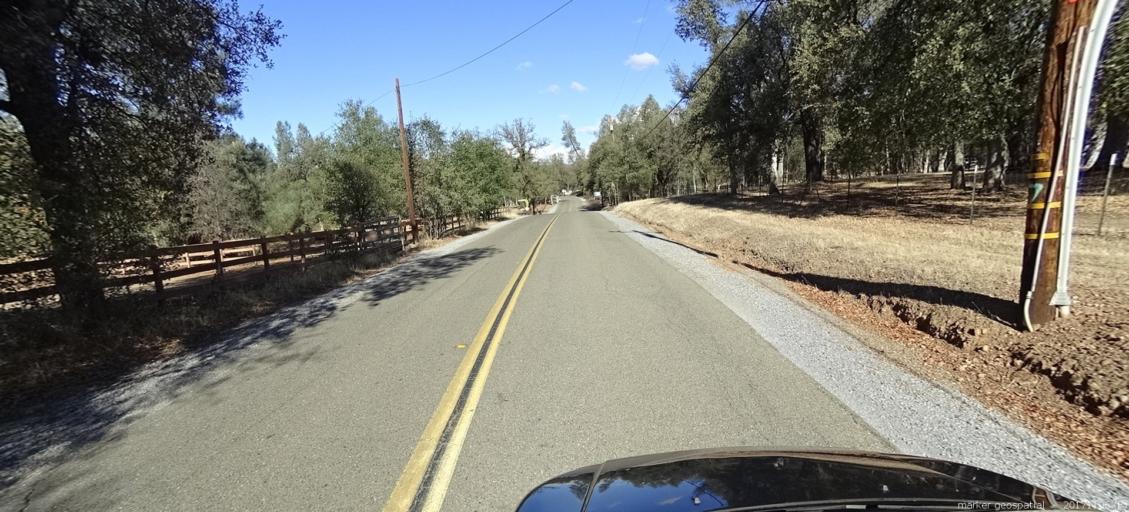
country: US
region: California
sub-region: Shasta County
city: Bella Vista
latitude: 40.6138
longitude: -122.2776
